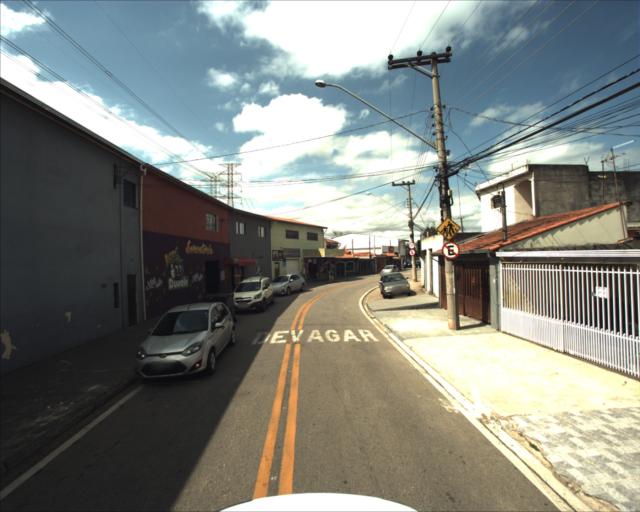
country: BR
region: Sao Paulo
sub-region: Sorocaba
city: Sorocaba
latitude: -23.3950
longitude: -47.3798
